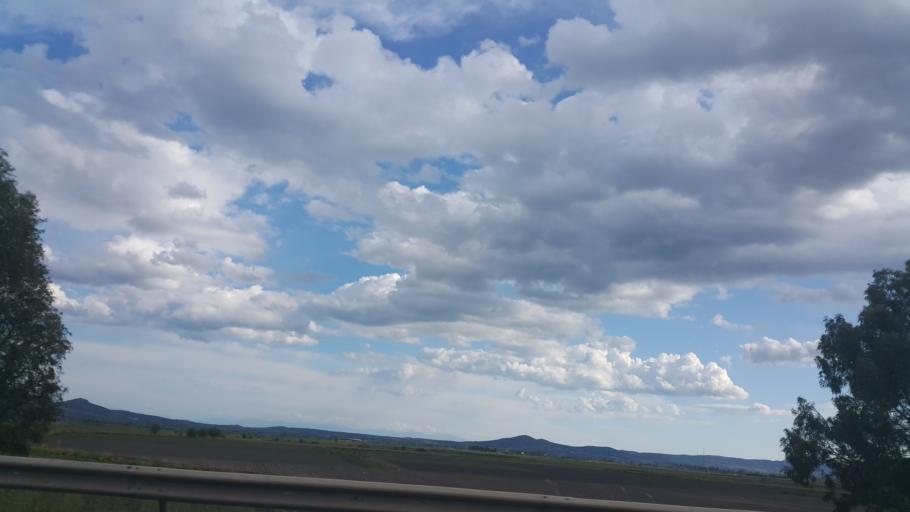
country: TR
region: Adana
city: Ceyhan
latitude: 36.9827
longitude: 35.8373
